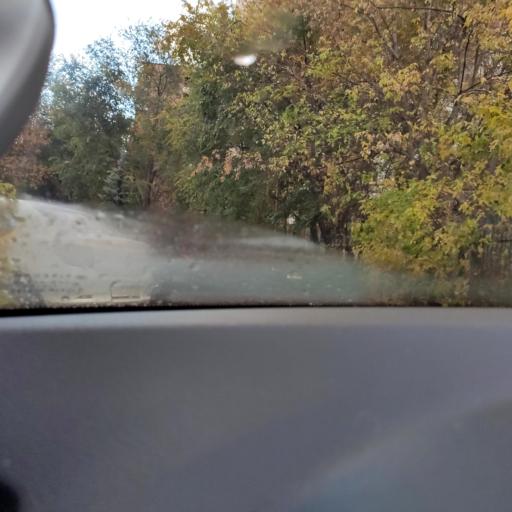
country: RU
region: Samara
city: Smyshlyayevka
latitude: 53.2068
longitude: 50.2843
